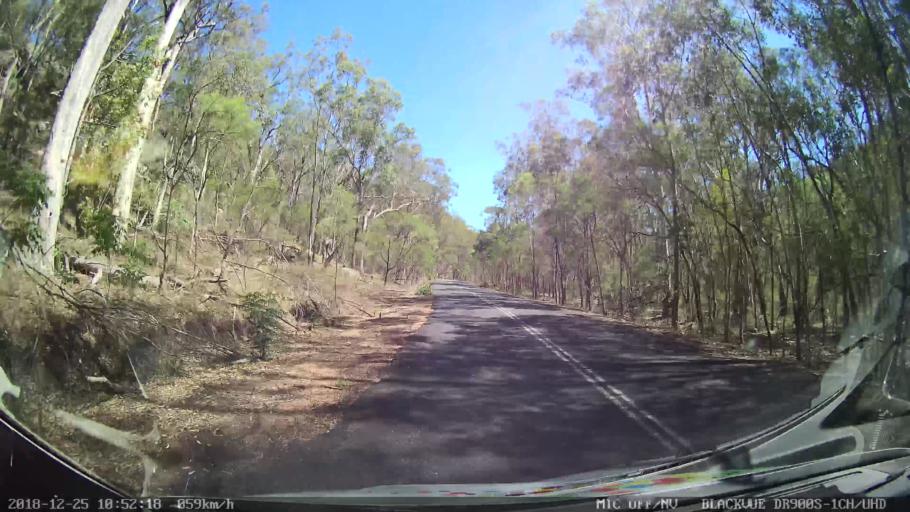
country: AU
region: New South Wales
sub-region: Upper Hunter Shire
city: Merriwa
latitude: -32.4299
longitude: 150.2736
